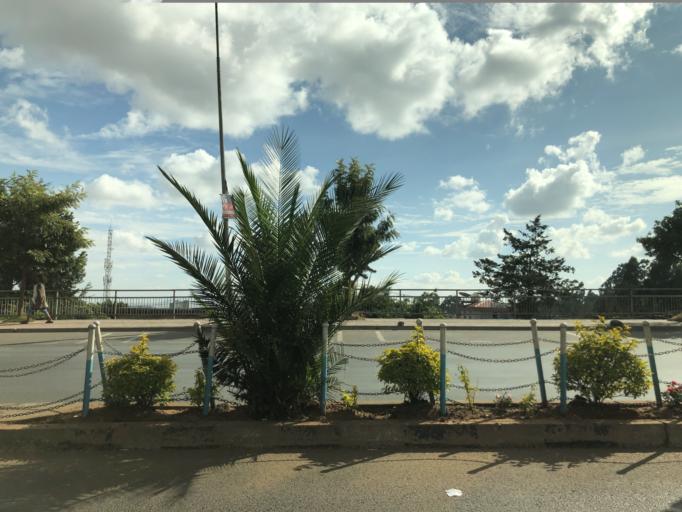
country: ET
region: Adis Abeba
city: Addis Ababa
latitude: 9.0315
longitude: 38.7706
